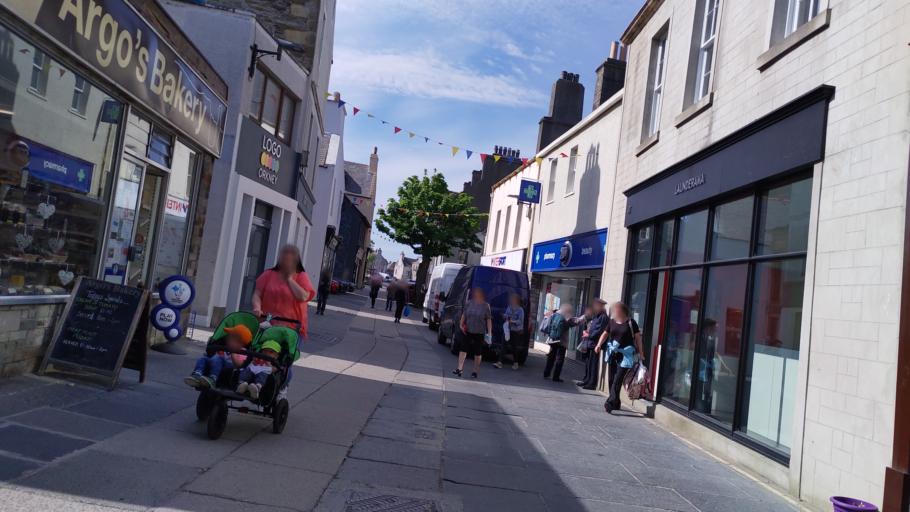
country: GB
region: Scotland
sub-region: Orkney Islands
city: Orkney
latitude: 58.9829
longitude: -2.9592
